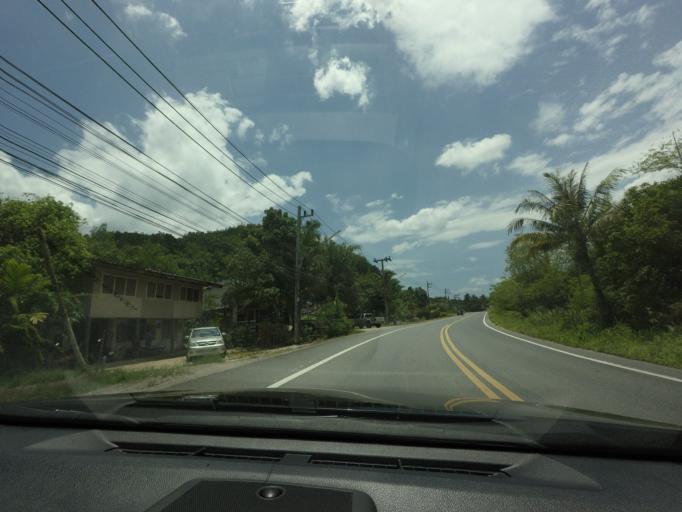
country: TH
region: Phangnga
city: Ban Khao Lak
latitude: 8.5455
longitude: 98.3616
